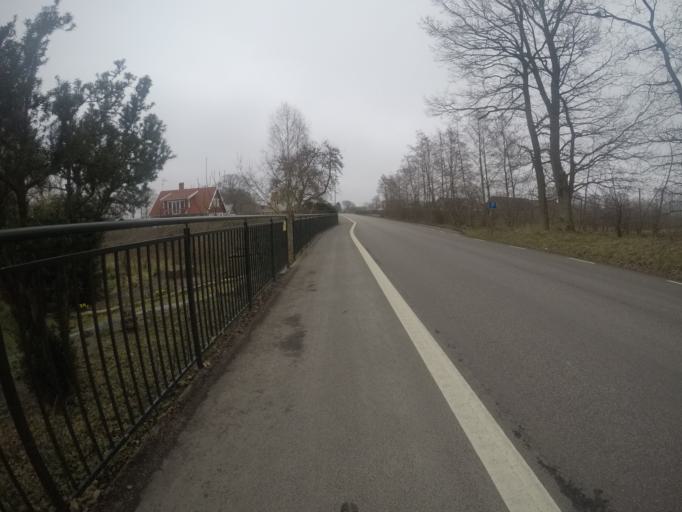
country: SE
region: Skane
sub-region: Angelholms Kommun
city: Strovelstorp
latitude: 56.2192
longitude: 12.7620
